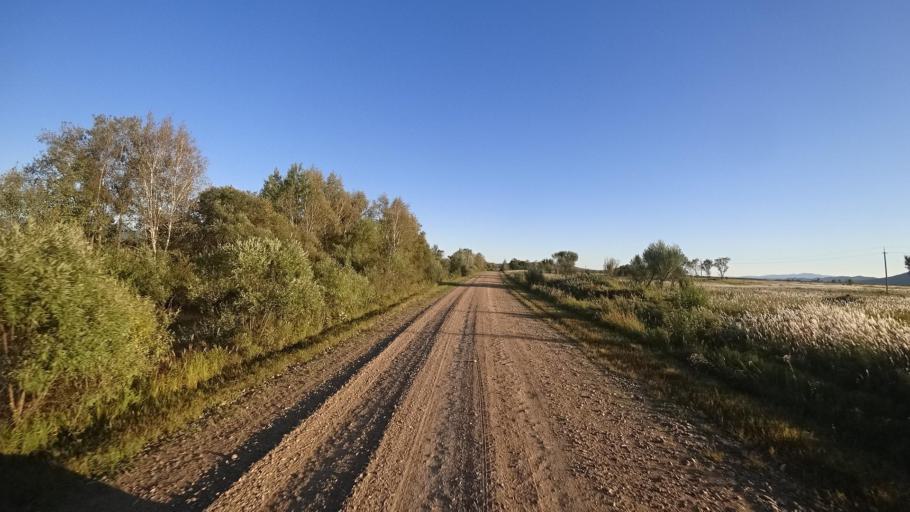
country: RU
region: Primorskiy
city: Kirovskiy
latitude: 44.8020
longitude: 133.6207
